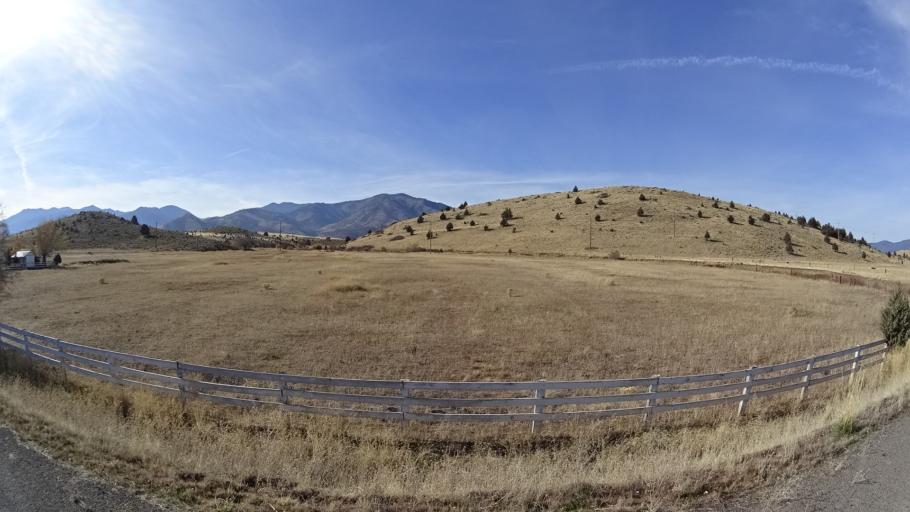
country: US
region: California
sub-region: Siskiyou County
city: Weed
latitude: 41.5035
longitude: -122.4560
